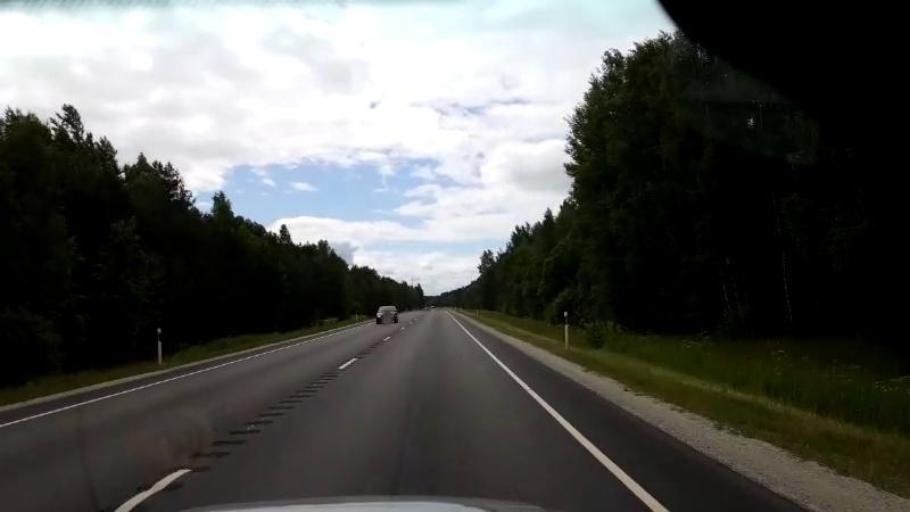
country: LV
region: Salacgrivas
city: Ainazi
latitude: 58.0951
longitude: 24.5079
